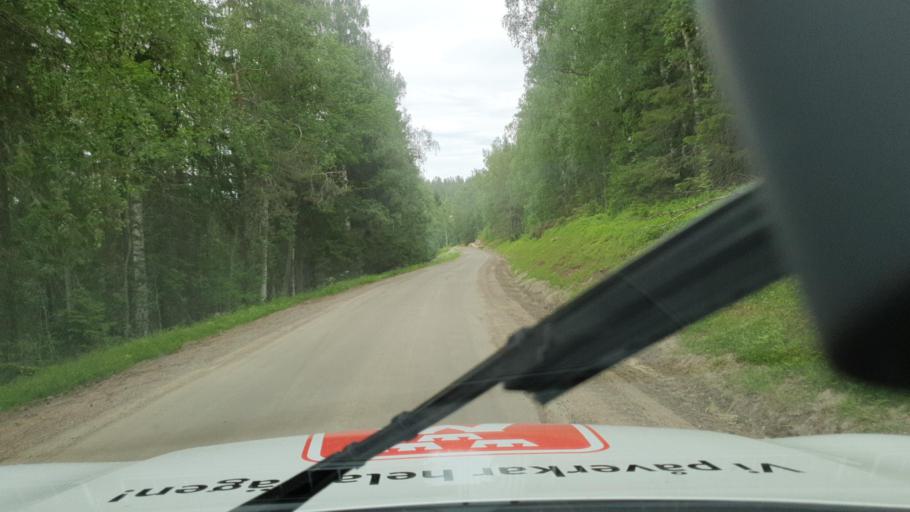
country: SE
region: Vaesterbotten
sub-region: Nordmalings Kommun
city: Nordmaling
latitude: 63.6798
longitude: 19.4471
